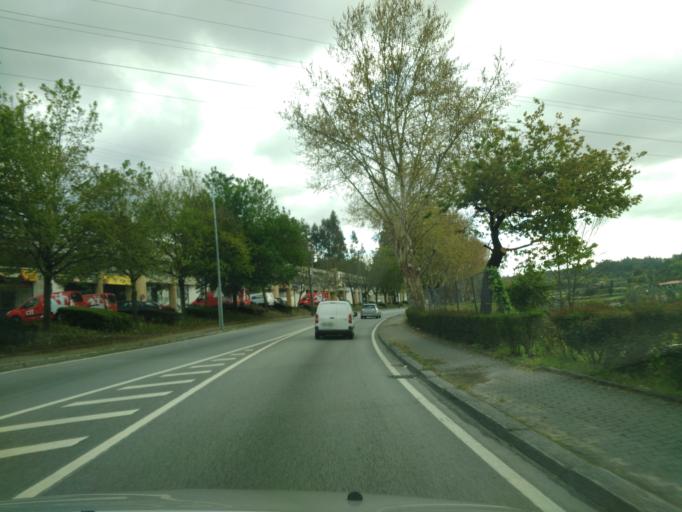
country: PT
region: Braga
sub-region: Guimaraes
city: Urgeses
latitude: 41.4298
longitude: -8.3023
